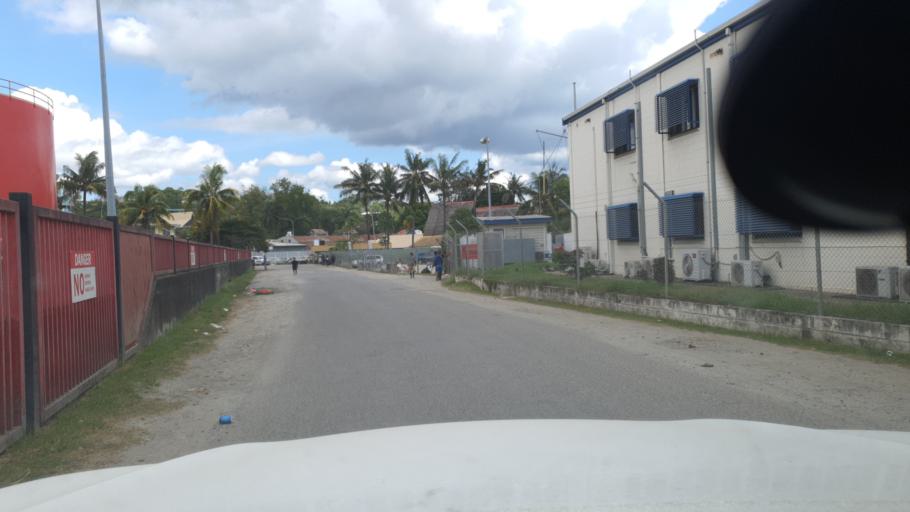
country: SB
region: Guadalcanal
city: Honiara
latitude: -9.4298
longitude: 159.9564
